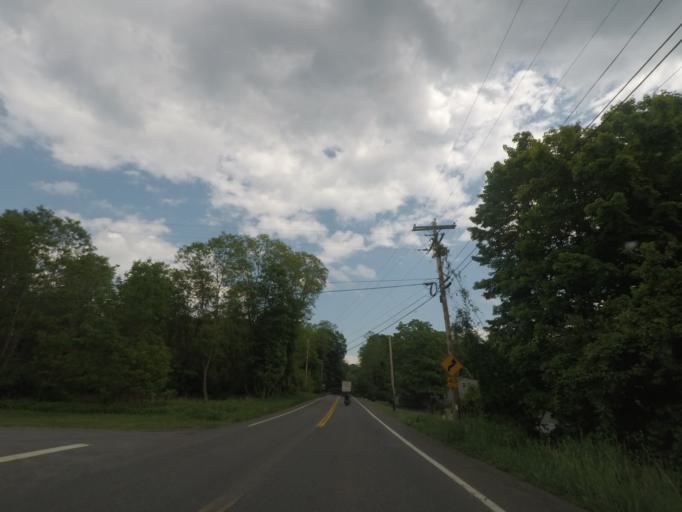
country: US
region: New York
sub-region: Dutchess County
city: Pine Plains
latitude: 42.0568
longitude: -73.6550
